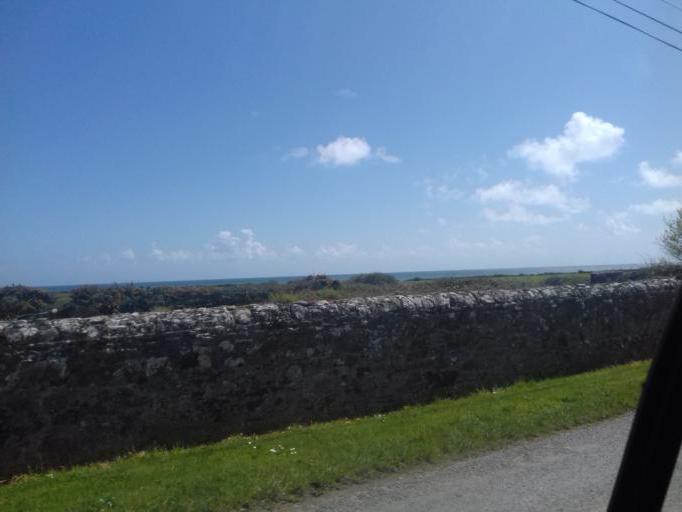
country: IE
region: Munster
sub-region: Waterford
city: Dunmore East
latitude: 52.1523
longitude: -6.9002
